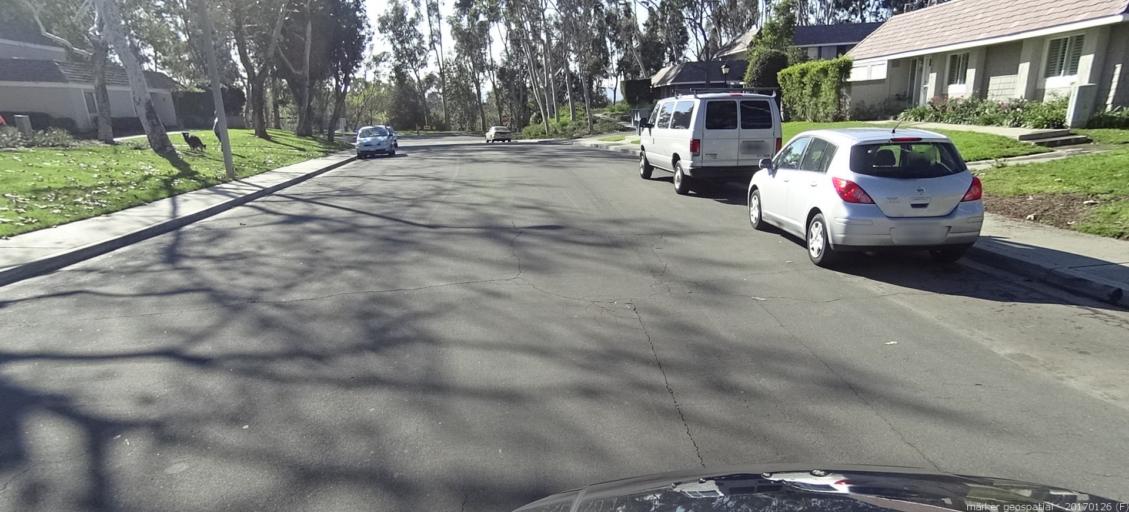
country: US
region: California
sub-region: Orange County
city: Lake Forest
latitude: 33.6436
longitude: -117.6972
